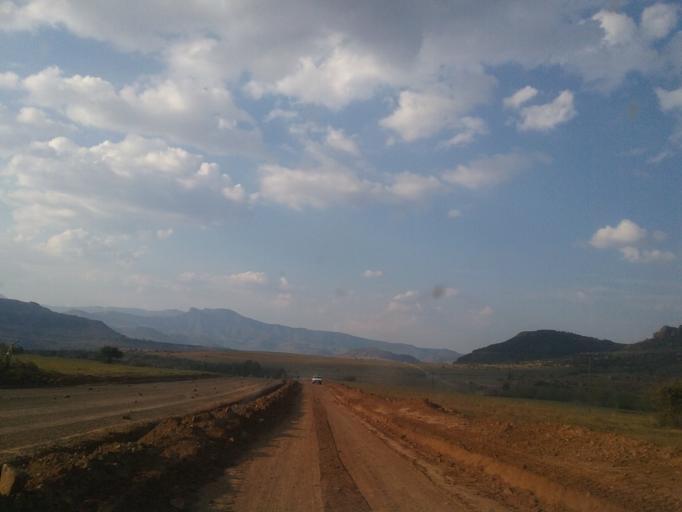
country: LS
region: Quthing
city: Quthing
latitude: -30.4133
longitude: 27.6000
